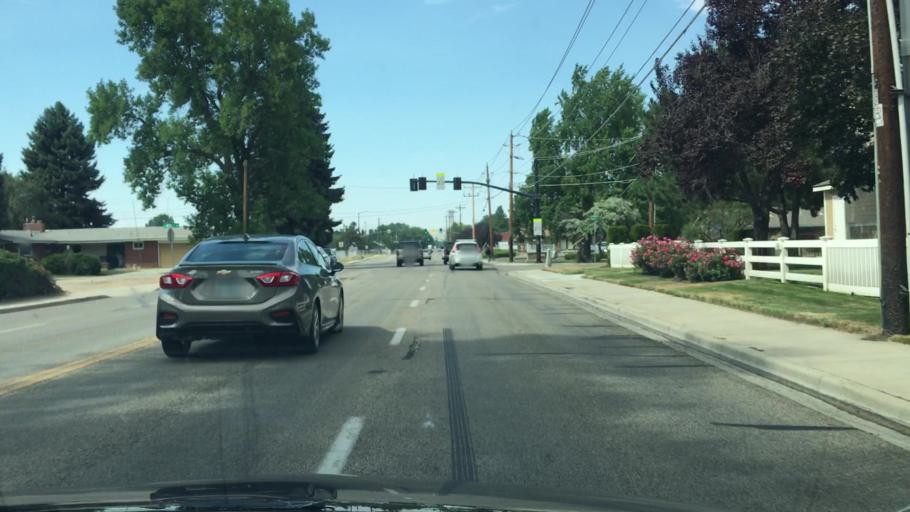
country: US
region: Idaho
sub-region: Ada County
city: Garden City
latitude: 43.6230
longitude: -116.2742
